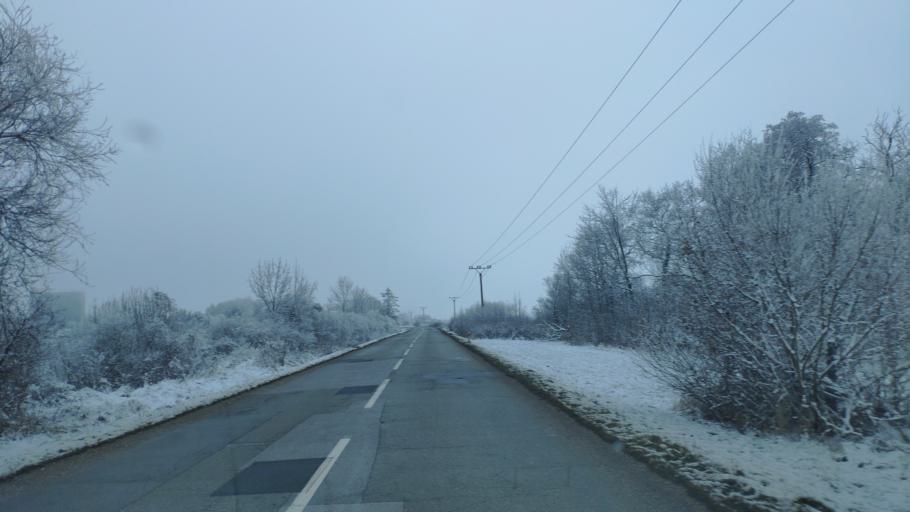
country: SK
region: Kosicky
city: Kosice
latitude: 48.6487
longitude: 21.1681
